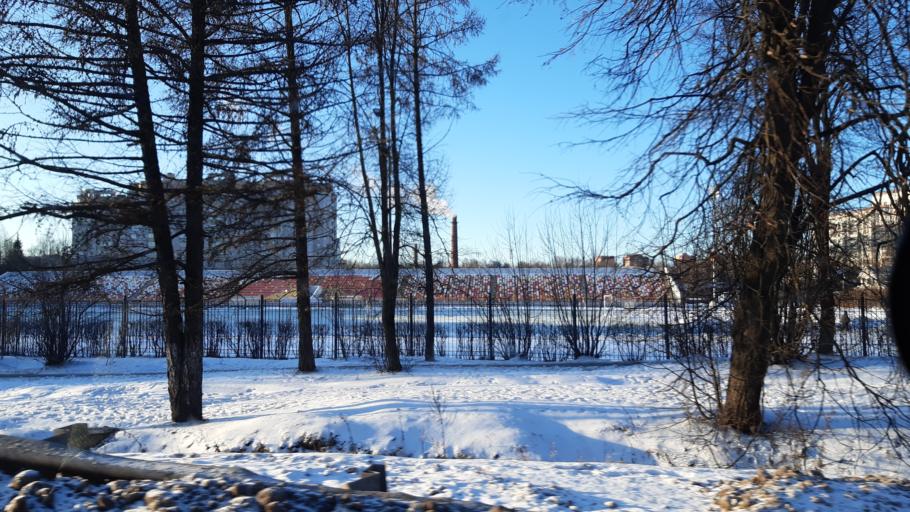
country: RU
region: Moskovskaya
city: Sergiyev Posad
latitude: 56.3260
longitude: 38.1487
